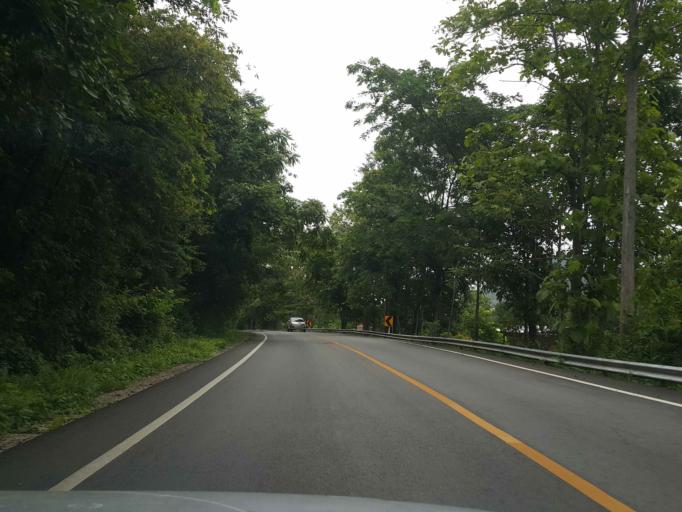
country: TH
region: Lampang
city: Thoen
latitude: 17.5528
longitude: 99.3384
